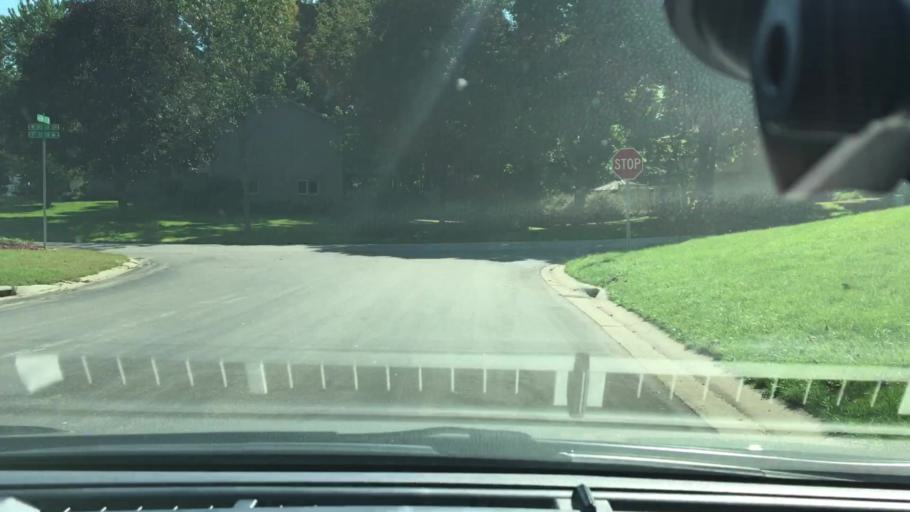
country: US
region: Minnesota
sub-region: Wright County
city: Saint Michael
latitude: 45.2037
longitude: -93.6743
